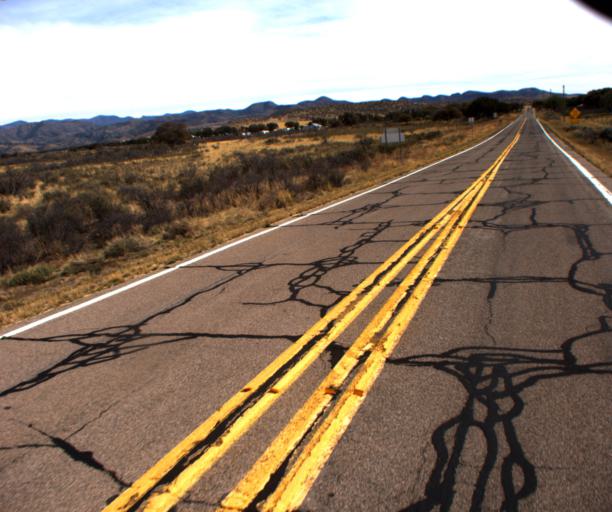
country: US
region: Arizona
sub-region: Cochise County
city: Willcox
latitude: 32.0057
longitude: -109.4400
